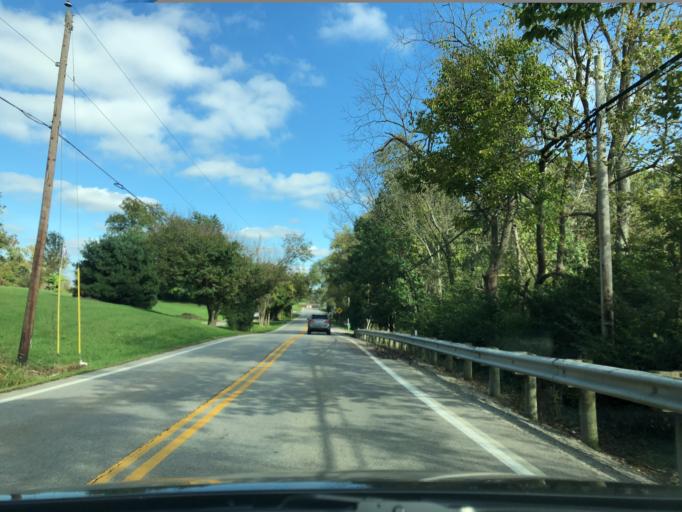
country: US
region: Ohio
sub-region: Hamilton County
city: Loveland
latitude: 39.2808
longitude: -84.2312
